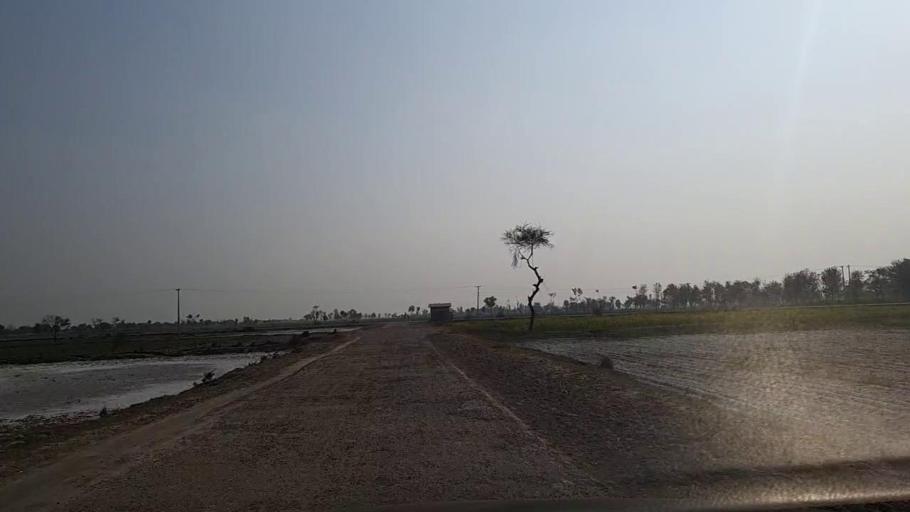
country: PK
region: Sindh
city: Daur
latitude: 26.4107
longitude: 68.4125
